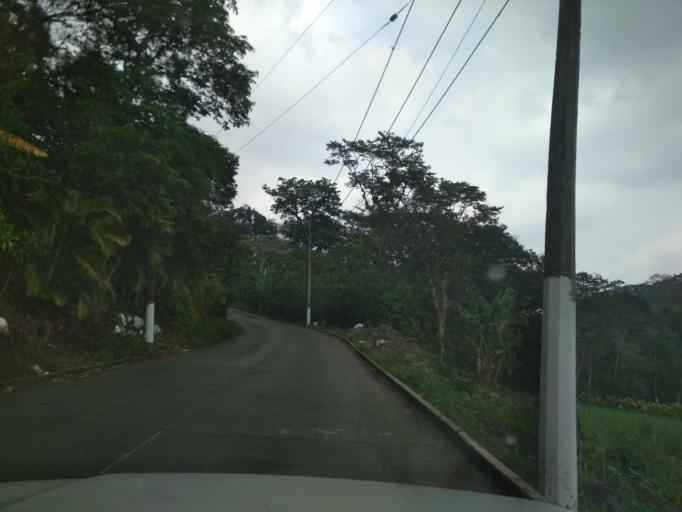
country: MX
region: Veracruz
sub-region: Cordoba
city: San Jose de Tapia
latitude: 18.8386
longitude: -96.9839
